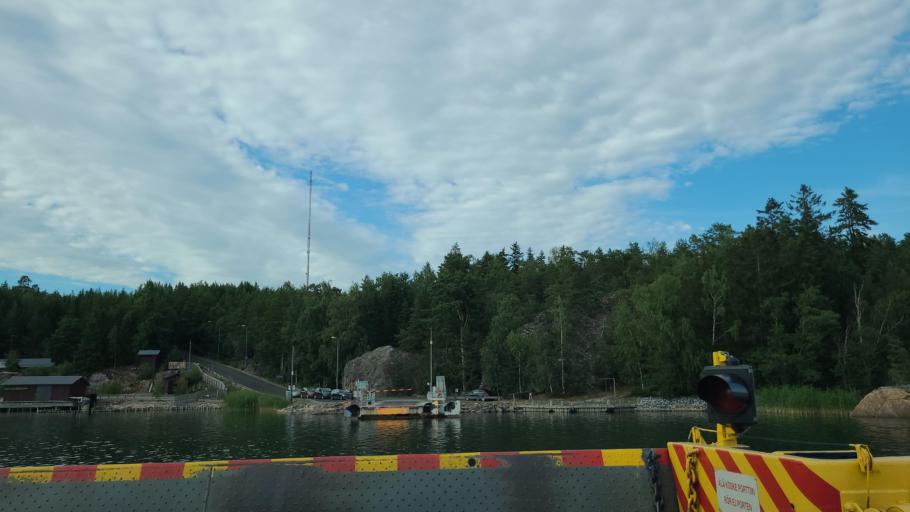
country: FI
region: Varsinais-Suomi
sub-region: Turku
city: Rymaettylae
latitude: 60.3157
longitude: 21.9629
